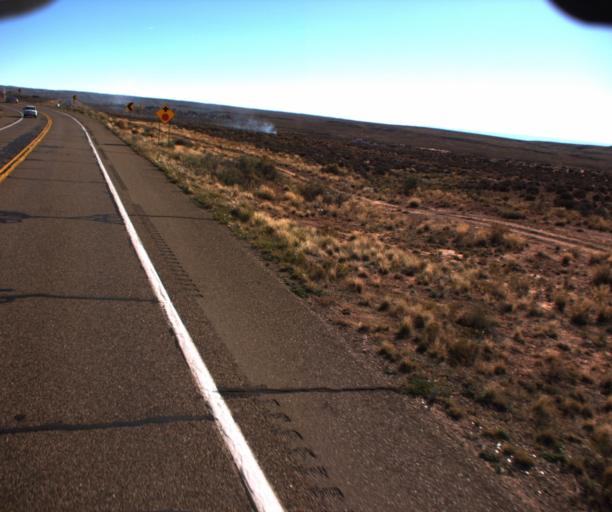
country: US
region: Arizona
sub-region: Coconino County
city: LeChee
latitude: 36.6372
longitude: -111.6525
